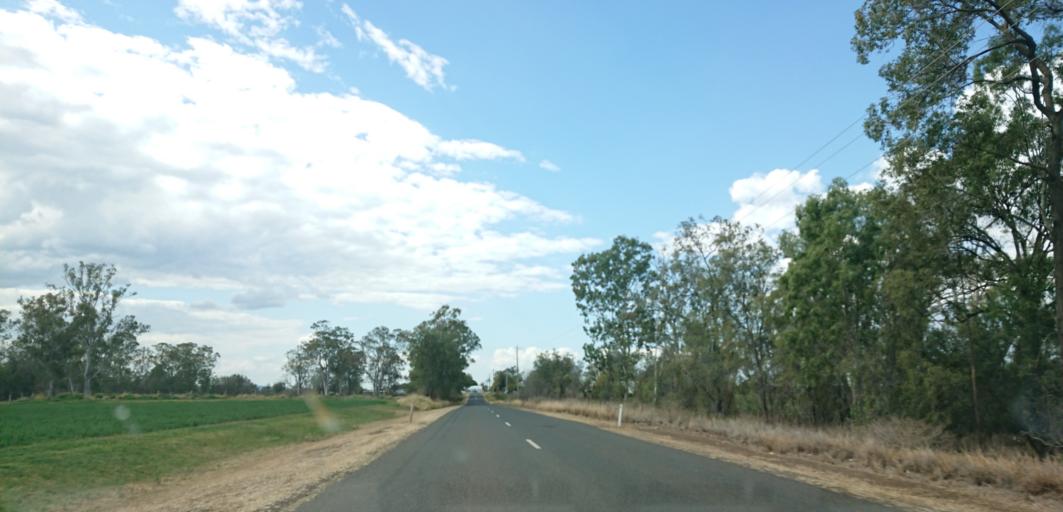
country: AU
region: Queensland
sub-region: Lockyer Valley
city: Gatton
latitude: -27.6011
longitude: 152.2178
